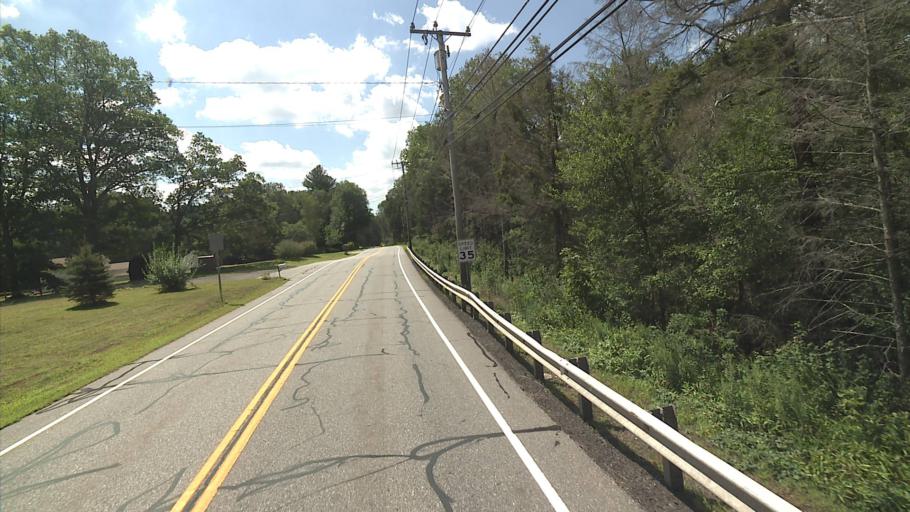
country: US
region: Connecticut
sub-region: Windham County
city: South Woodstock
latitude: 41.8860
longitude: -72.0825
